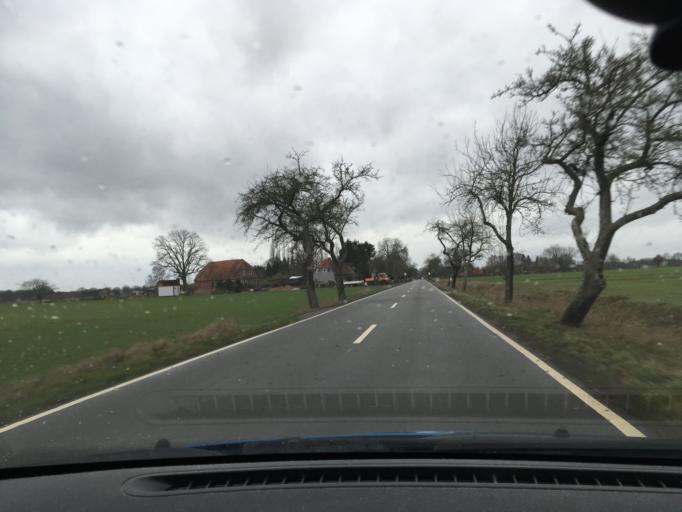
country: DE
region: Mecklenburg-Vorpommern
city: Boizenburg
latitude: 53.3483
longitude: 10.6942
